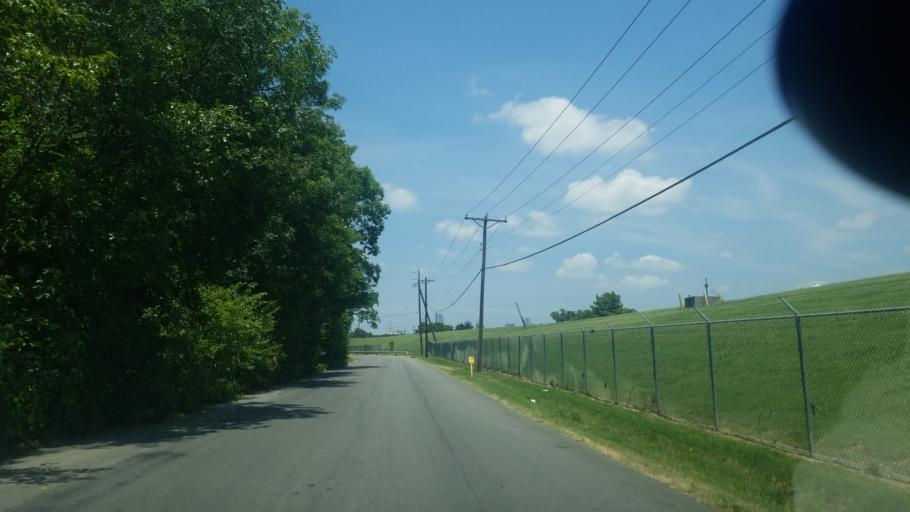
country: US
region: Texas
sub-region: Dallas County
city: Dallas
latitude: 32.7327
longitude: -96.7760
